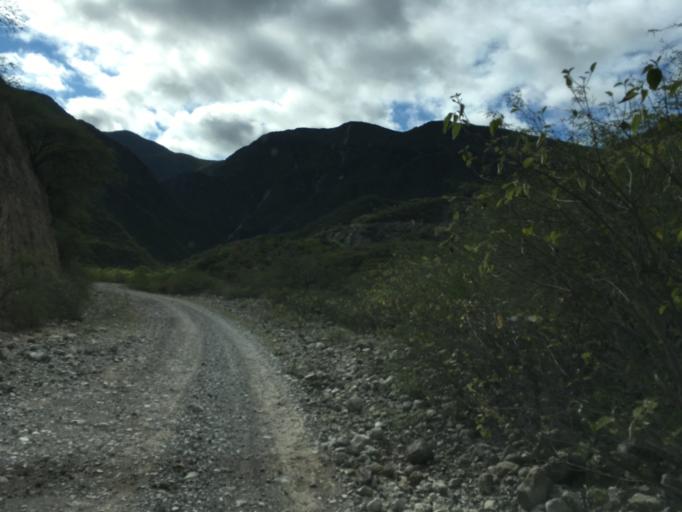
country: MX
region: Hidalgo
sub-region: Metztitlan
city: Fontezuelas
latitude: 20.6388
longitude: -98.9291
